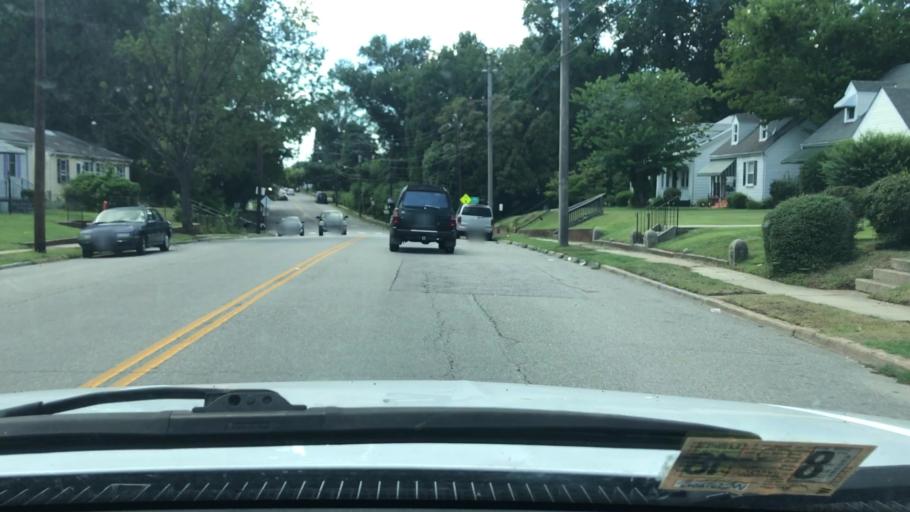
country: US
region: Virginia
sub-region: Henrico County
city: East Highland Park
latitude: 37.5711
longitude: -77.4261
